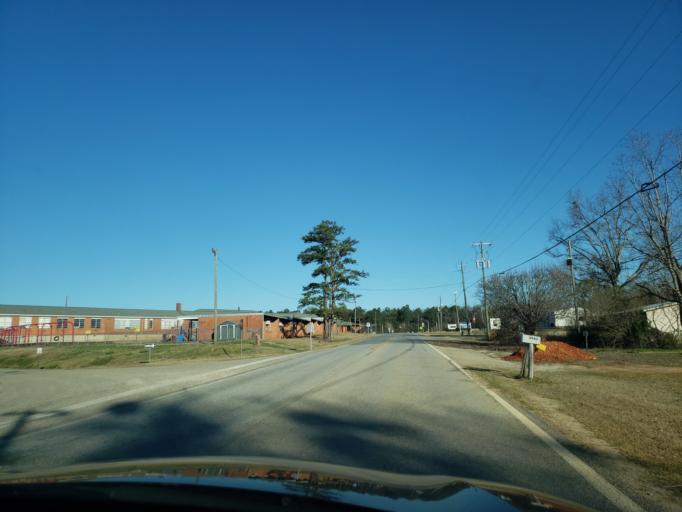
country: US
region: Alabama
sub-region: Elmore County
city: Tallassee
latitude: 32.6013
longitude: -85.8034
